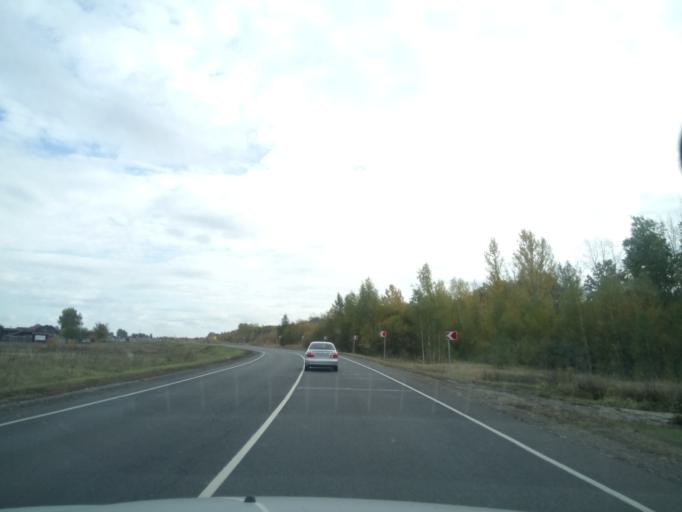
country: RU
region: Nizjnij Novgorod
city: Lukoyanov
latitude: 55.0504
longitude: 44.3768
